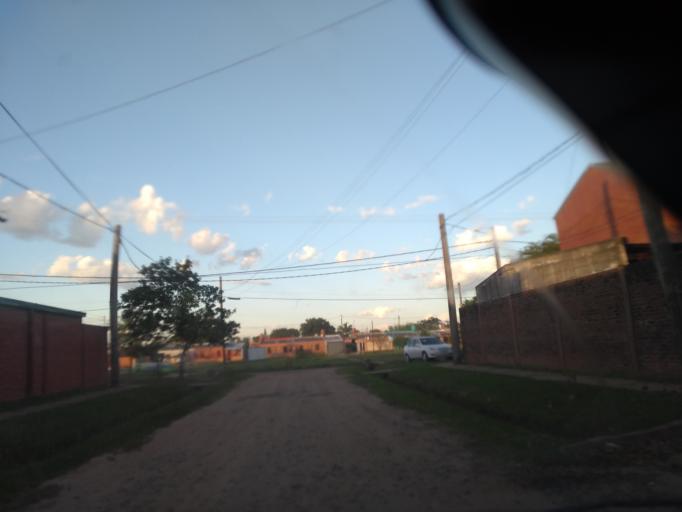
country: AR
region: Chaco
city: Resistencia
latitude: -27.4521
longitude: -58.9637
